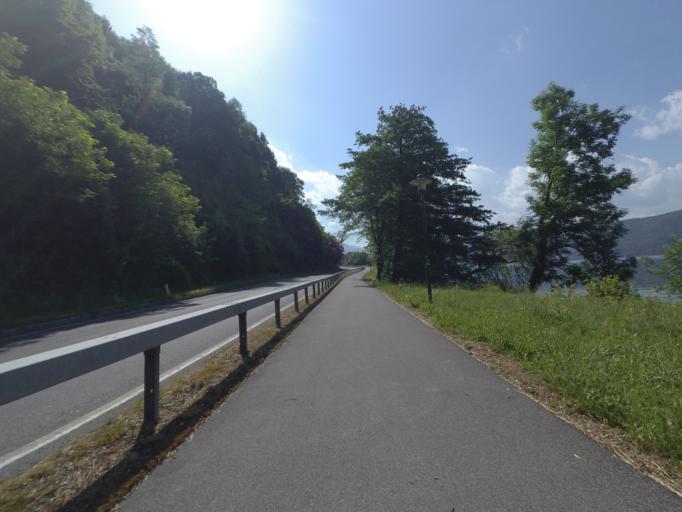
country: AT
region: Carinthia
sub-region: Politischer Bezirk Spittal an der Drau
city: Millstatt
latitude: 46.7924
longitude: 13.6069
